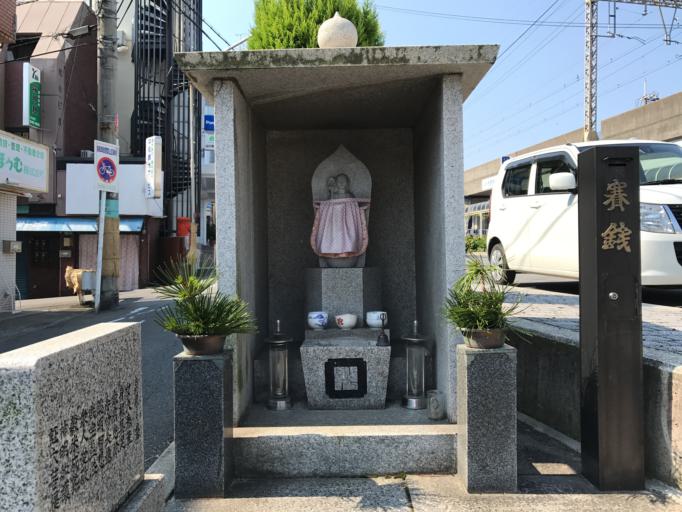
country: JP
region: Osaka
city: Kashihara
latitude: 34.6087
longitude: 135.6267
